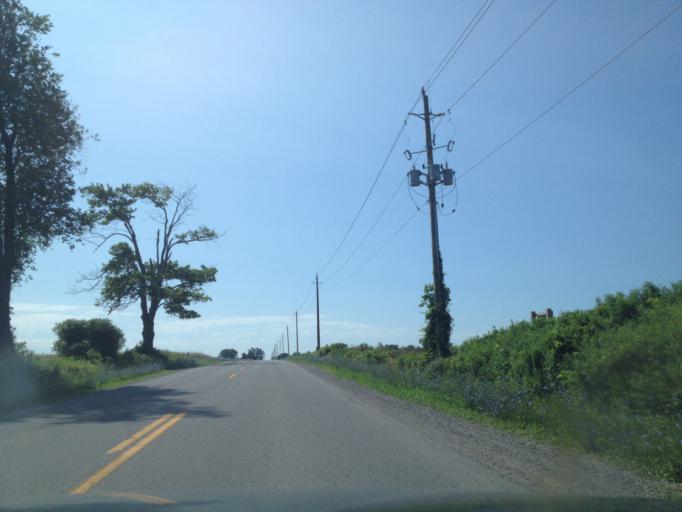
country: CA
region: Ontario
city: Norfolk County
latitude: 42.7507
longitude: -80.3778
